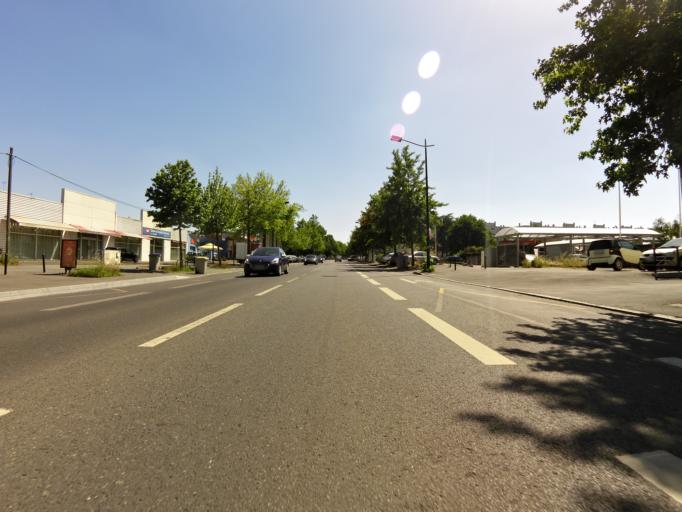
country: FR
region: Pays de la Loire
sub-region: Departement de la Loire-Atlantique
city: Saint-Herblain
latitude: 47.2202
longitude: -1.6034
